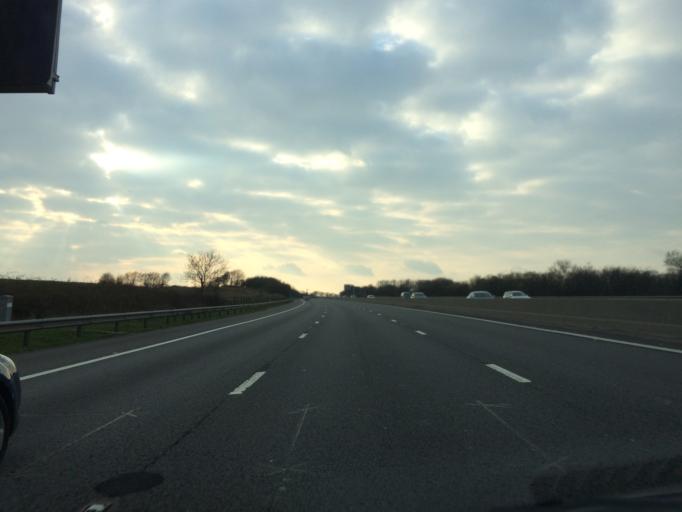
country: GB
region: England
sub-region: Wiltshire
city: Aldbourne
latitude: 51.5063
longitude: -1.5992
